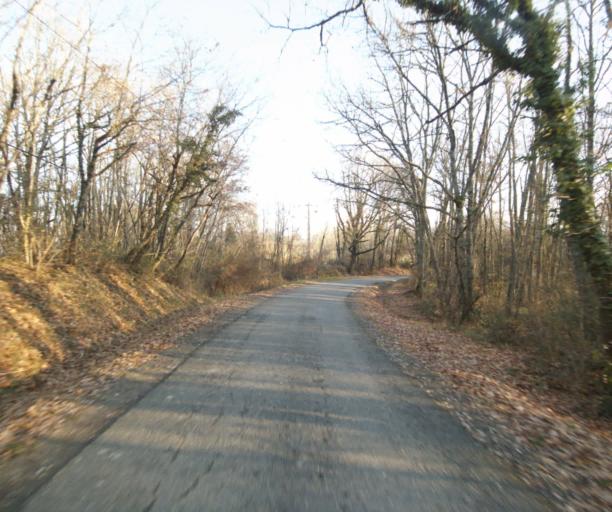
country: FR
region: Midi-Pyrenees
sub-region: Departement du Tarn-et-Garonne
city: Moissac
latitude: 44.1534
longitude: 1.1412
